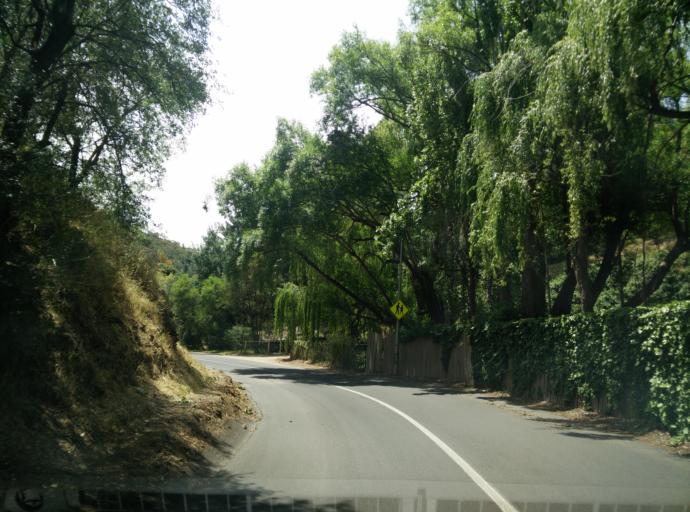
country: AU
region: South Australia
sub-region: Burnside
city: Beaumont
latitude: -34.9585
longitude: 138.6750
